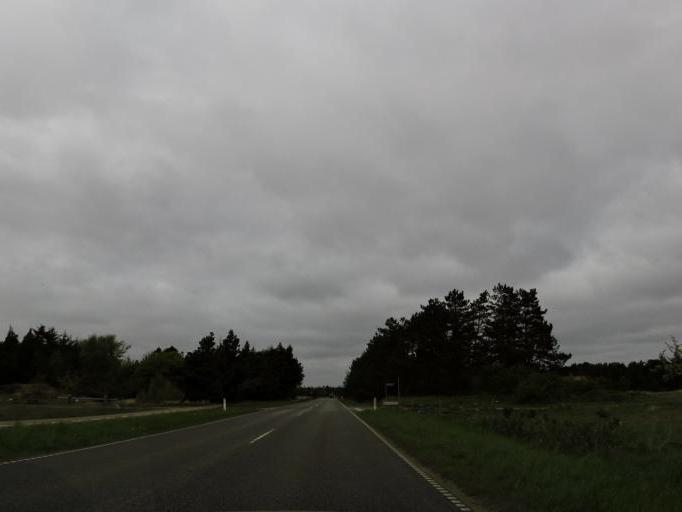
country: DE
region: Schleswig-Holstein
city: List
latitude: 55.1042
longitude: 8.5422
